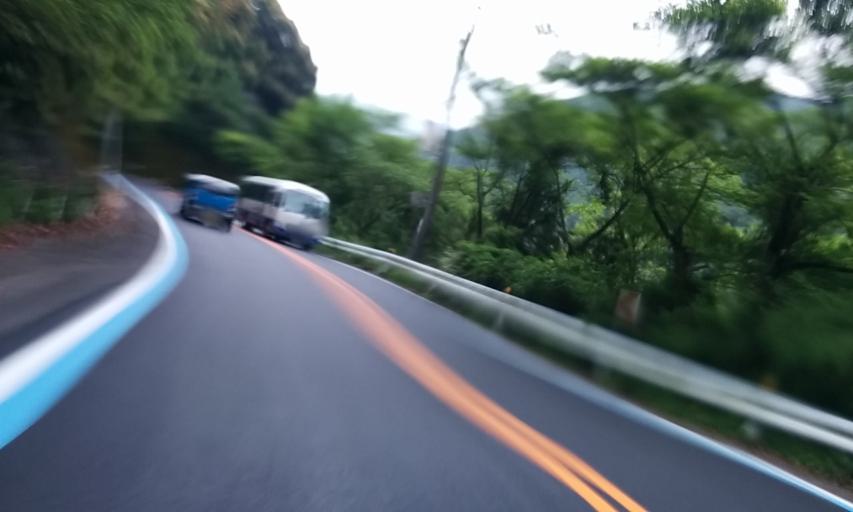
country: JP
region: Ehime
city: Niihama
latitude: 33.9080
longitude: 133.3074
